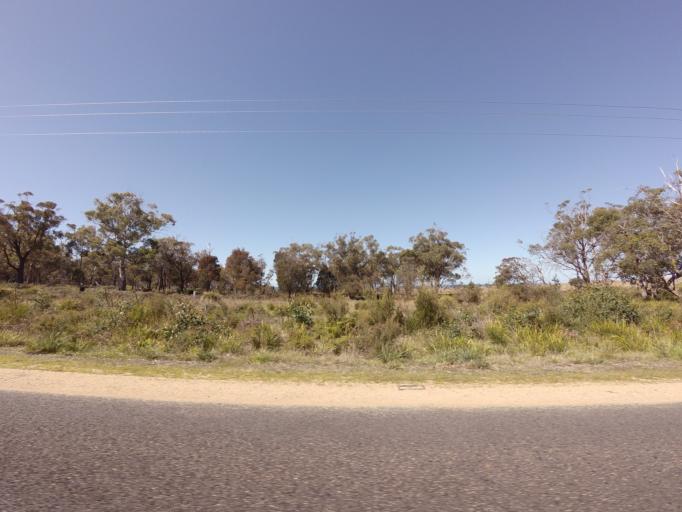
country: AU
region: Tasmania
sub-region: Break O'Day
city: St Helens
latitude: -41.6982
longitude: 148.2770
